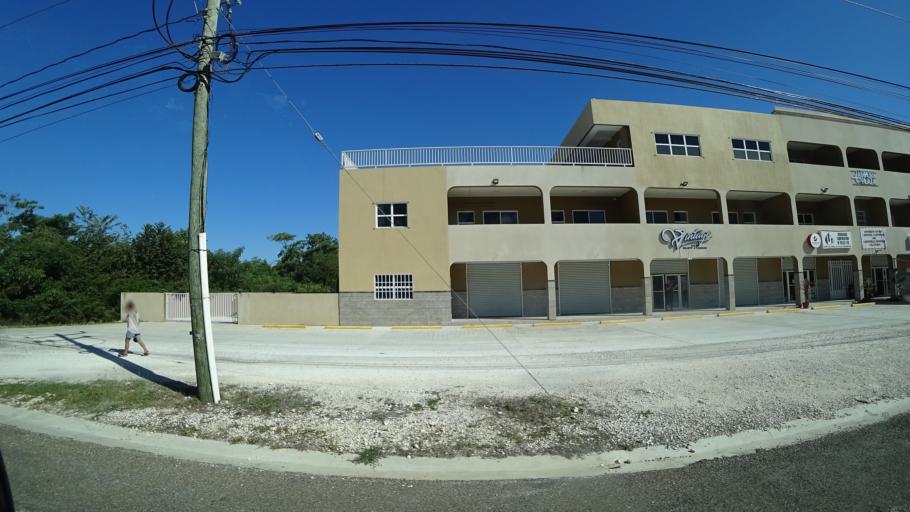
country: BZ
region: Belize
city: Belize City
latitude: 17.5458
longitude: -88.2861
